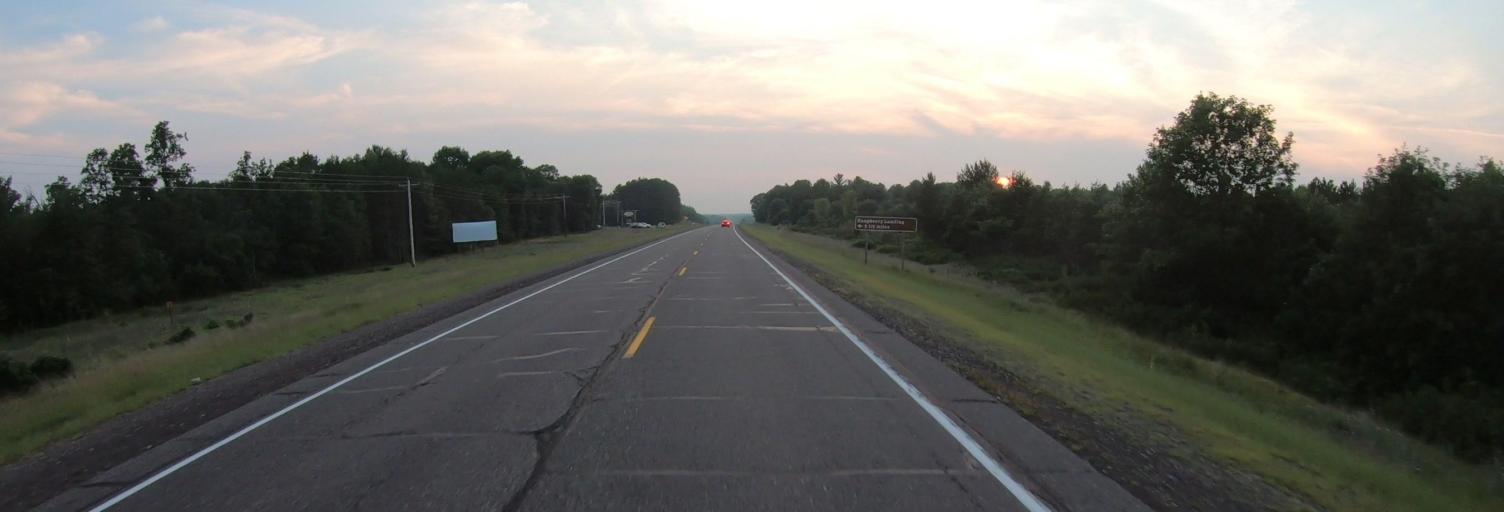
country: US
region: Wisconsin
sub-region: Burnett County
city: Grantsburg
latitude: 45.7730
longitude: -92.7603
